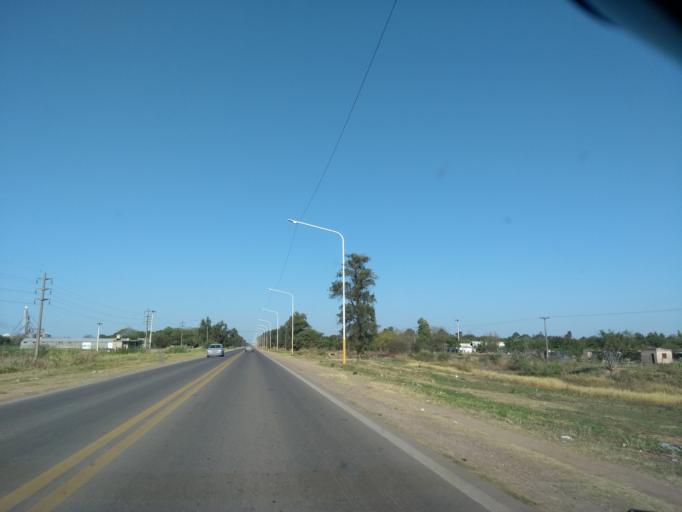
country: AR
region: Chaco
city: Presidencia Roque Saenz Pena
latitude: -26.7853
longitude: -60.4064
